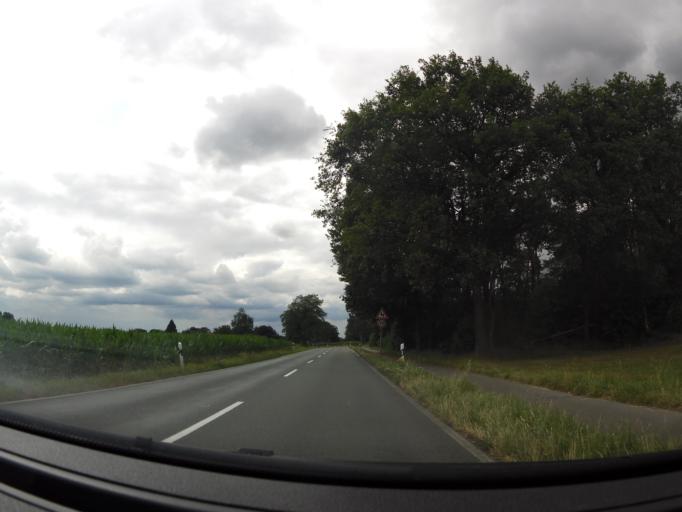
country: DE
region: North Rhine-Westphalia
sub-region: Regierungsbezirk Dusseldorf
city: Issum
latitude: 51.5819
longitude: 6.4141
